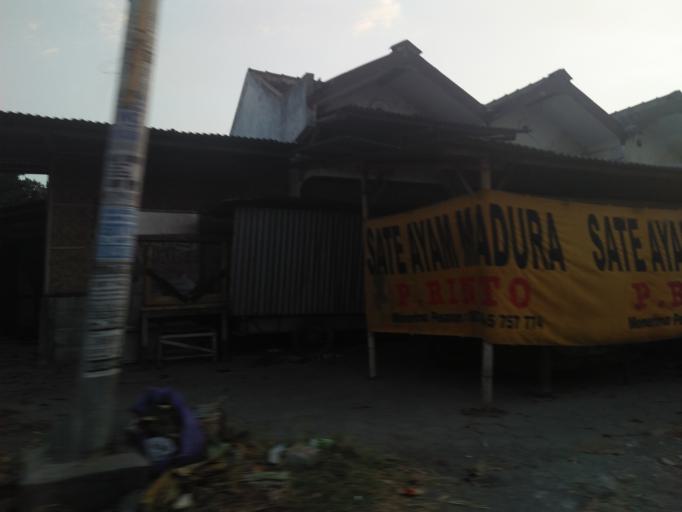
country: ID
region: Daerah Istimewa Yogyakarta
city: Sewon
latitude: -7.8472
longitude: 110.4078
